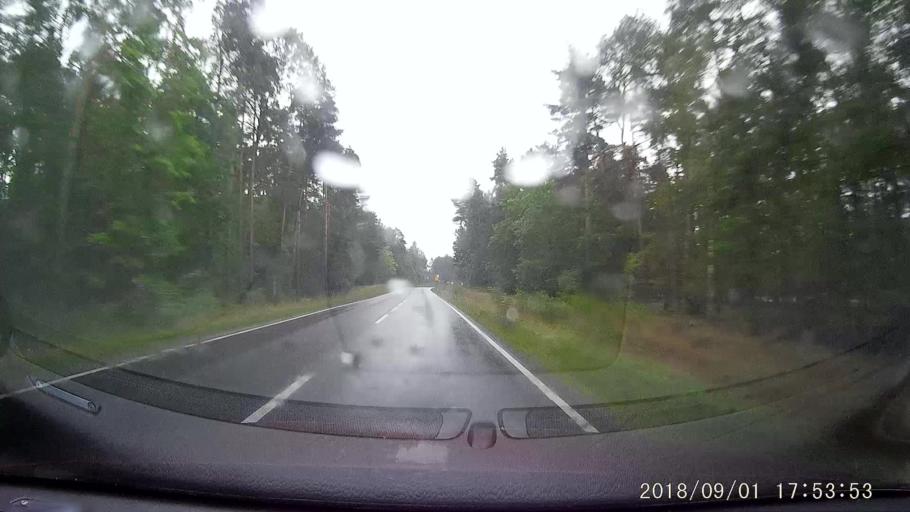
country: PL
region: Lubusz
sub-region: Powiat zaganski
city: Ilowa
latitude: 51.4744
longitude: 15.1992
